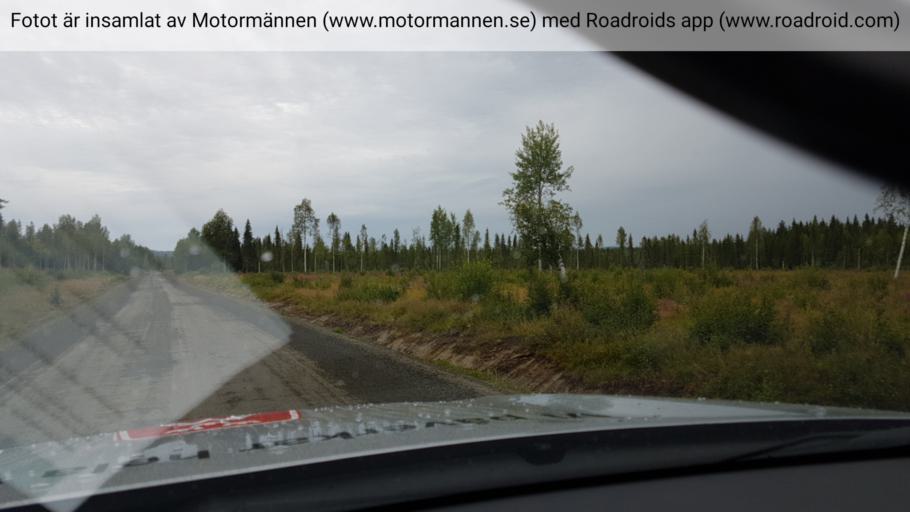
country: SE
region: Norrbotten
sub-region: Alvsbyns Kommun
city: AElvsbyn
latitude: 65.9215
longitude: 21.2650
